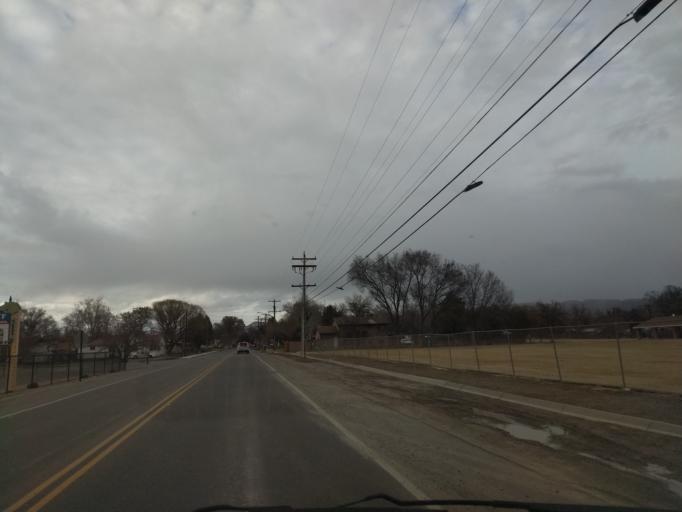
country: US
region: Colorado
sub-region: Mesa County
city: Fruitvale
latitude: 39.0829
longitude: -108.5199
